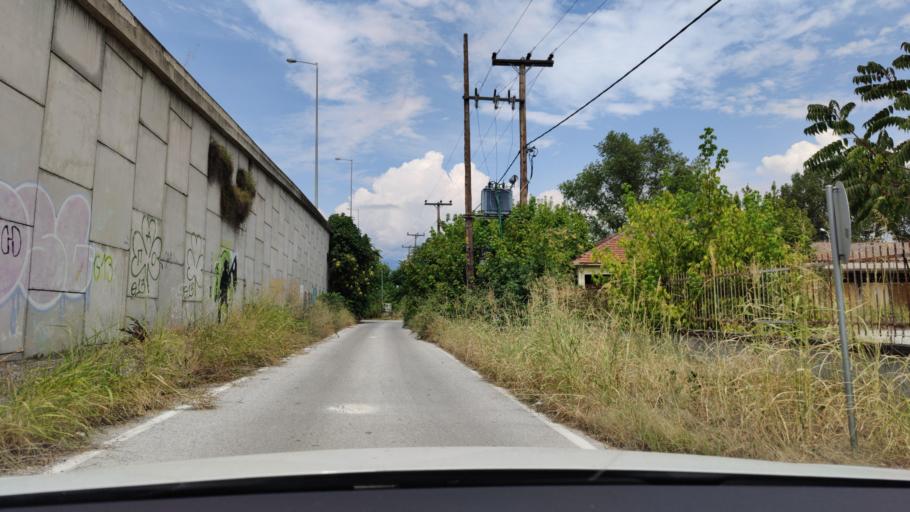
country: GR
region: Central Macedonia
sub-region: Nomos Serron
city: Serres
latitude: 41.0729
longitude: 23.5406
